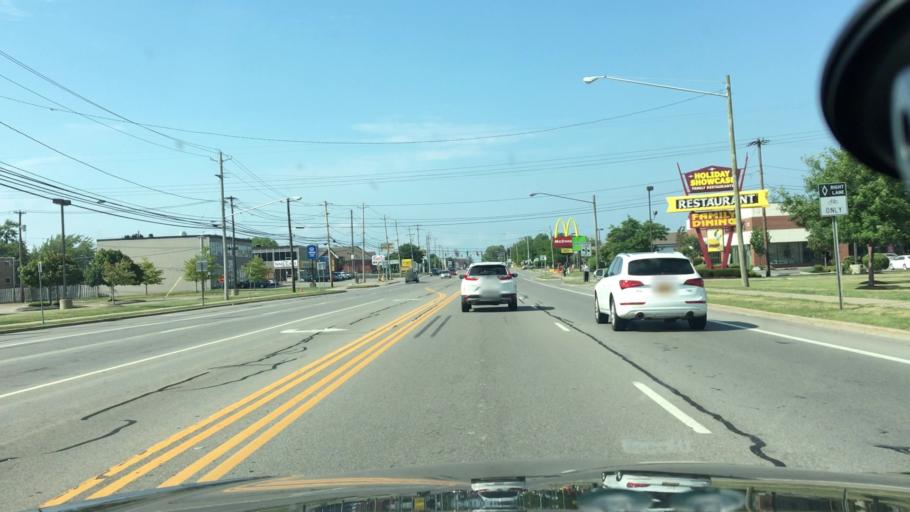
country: US
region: New York
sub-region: Erie County
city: Cheektowaga
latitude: 42.9163
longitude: -78.7541
